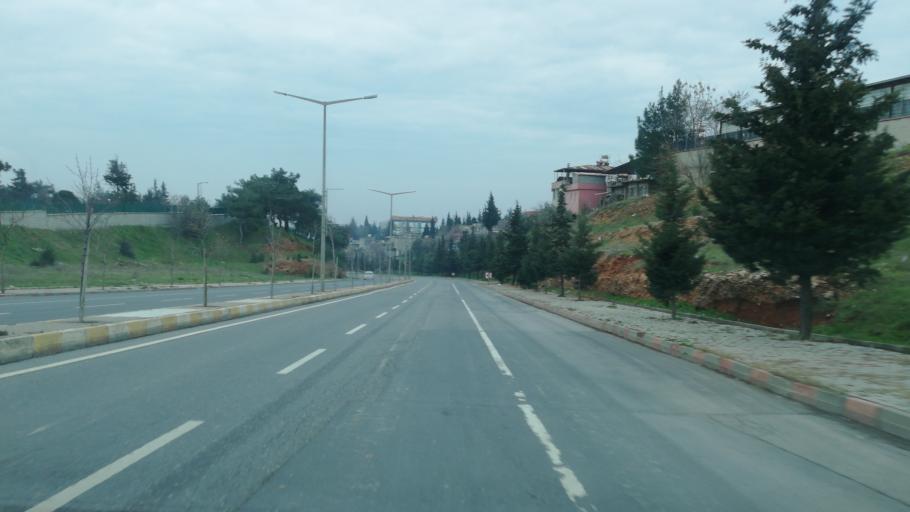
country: TR
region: Kahramanmaras
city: Kahramanmaras
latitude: 37.5966
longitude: 36.9251
